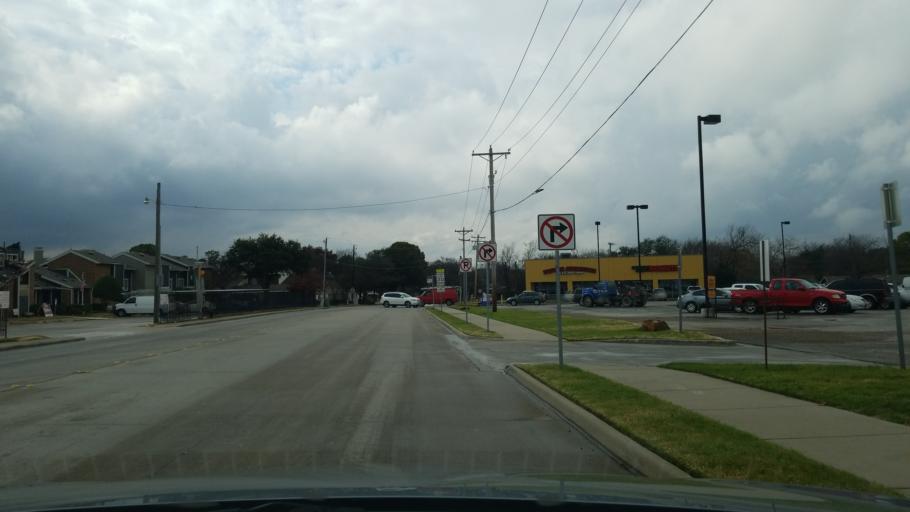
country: US
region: Texas
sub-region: Denton County
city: Lewisville
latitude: 33.0370
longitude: -97.0036
